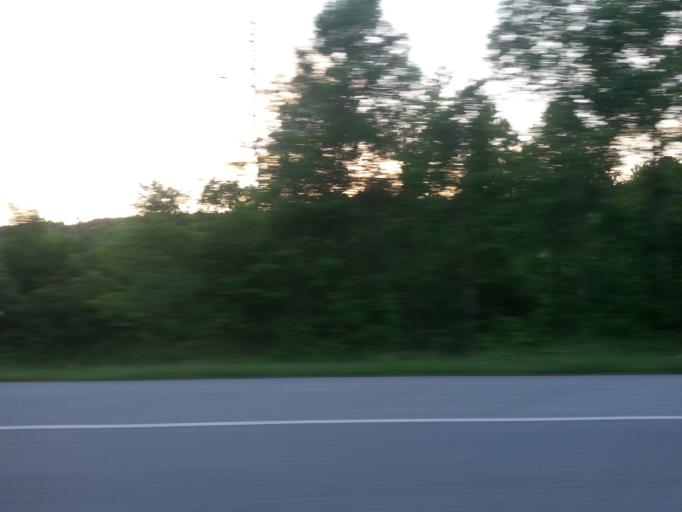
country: US
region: Tennessee
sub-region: Monroe County
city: Madisonville
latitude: 35.3581
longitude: -84.3015
